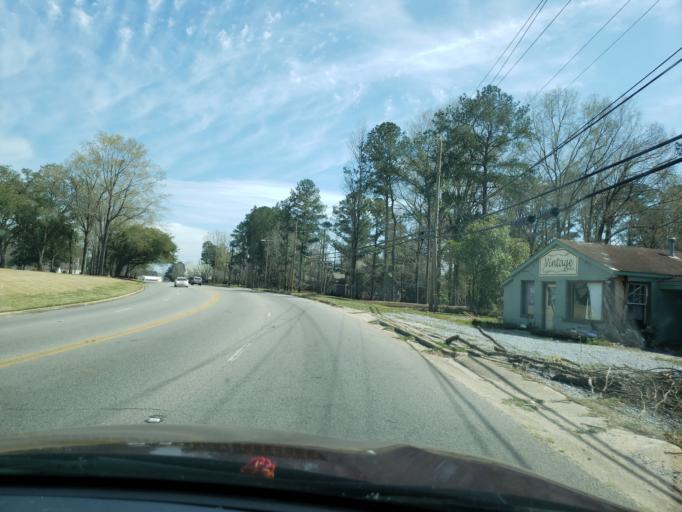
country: US
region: Alabama
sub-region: Elmore County
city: Tallassee
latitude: 32.5446
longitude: -85.9101
